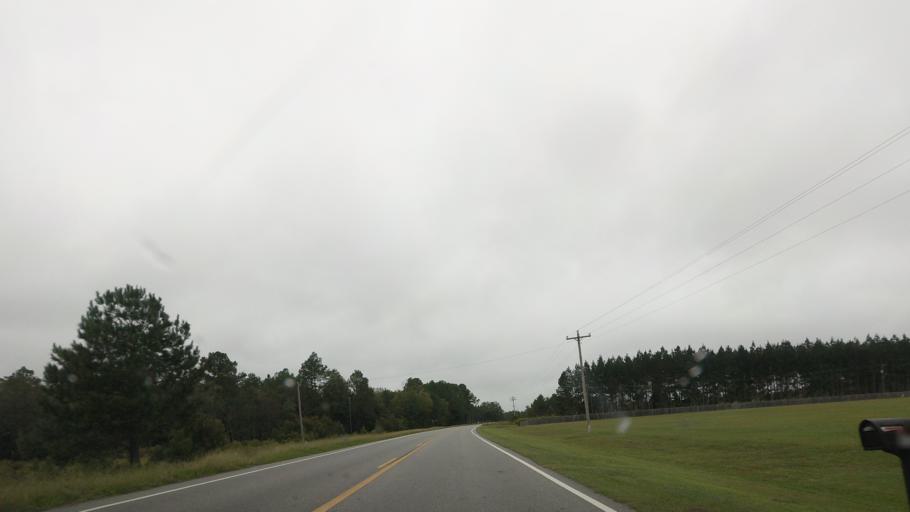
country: US
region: Georgia
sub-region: Berrien County
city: Nashville
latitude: 31.2835
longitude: -83.2393
